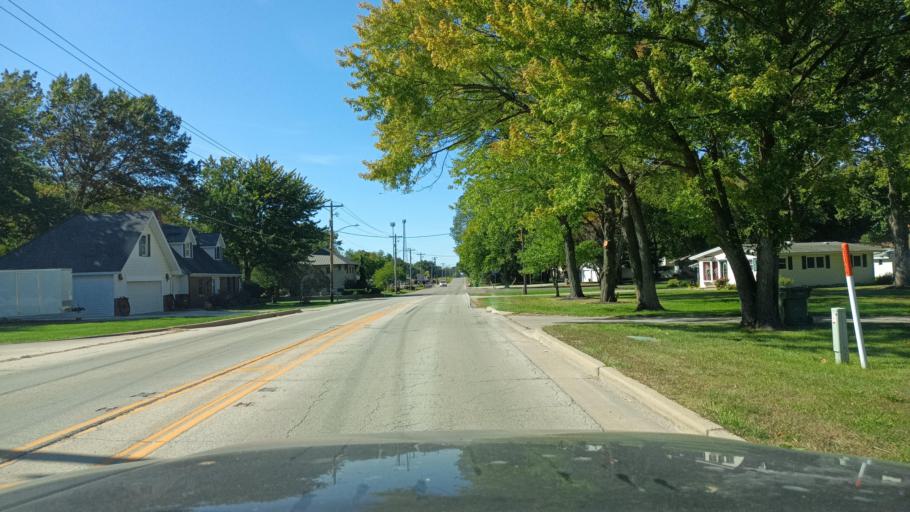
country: US
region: Illinois
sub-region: Champaign County
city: Mahomet
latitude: 40.1921
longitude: -88.4110
